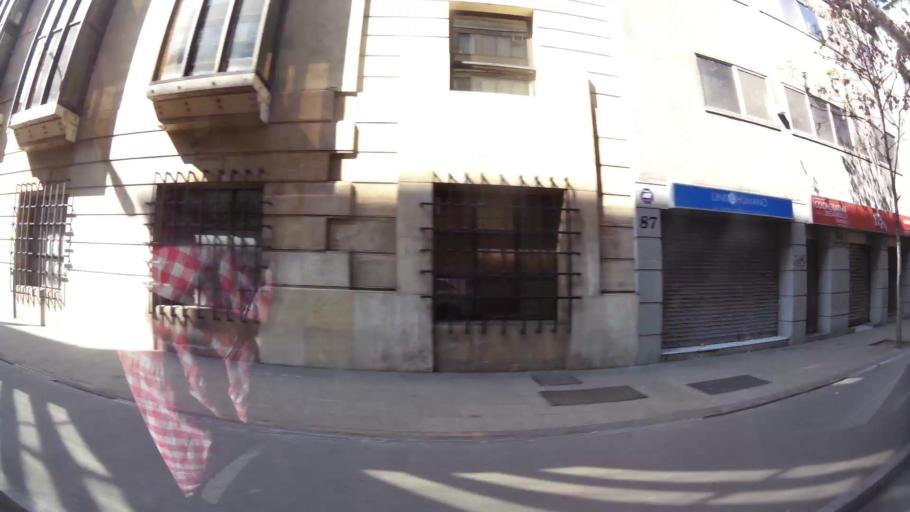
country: CL
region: Santiago Metropolitan
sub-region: Provincia de Santiago
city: Santiago
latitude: -33.4432
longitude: -70.6556
